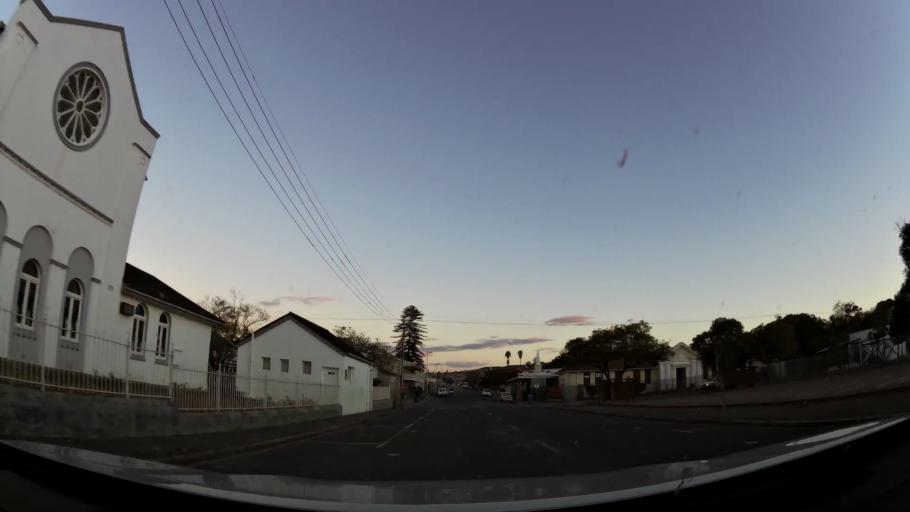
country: ZA
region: Western Cape
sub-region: Eden District Municipality
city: Riversdale
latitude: -34.0909
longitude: 21.2601
